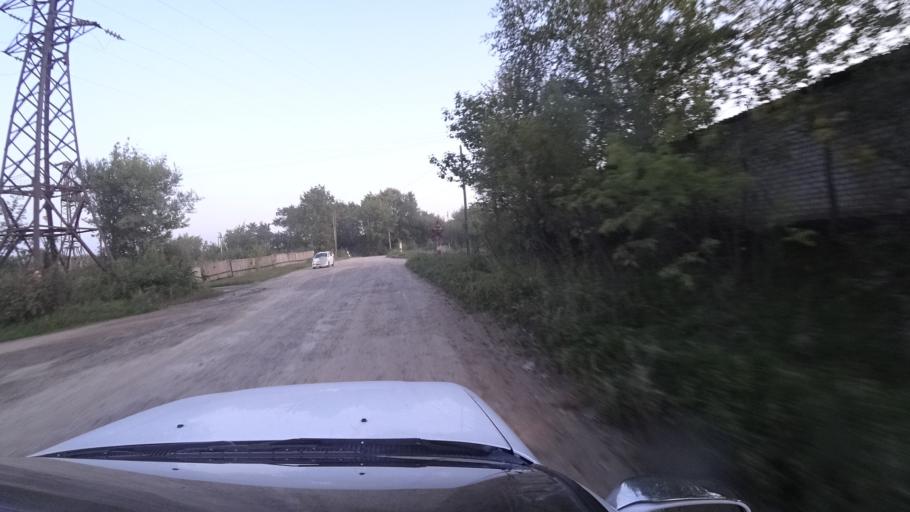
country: RU
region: Primorskiy
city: Dal'nerechensk
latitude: 45.9335
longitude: 133.7582
